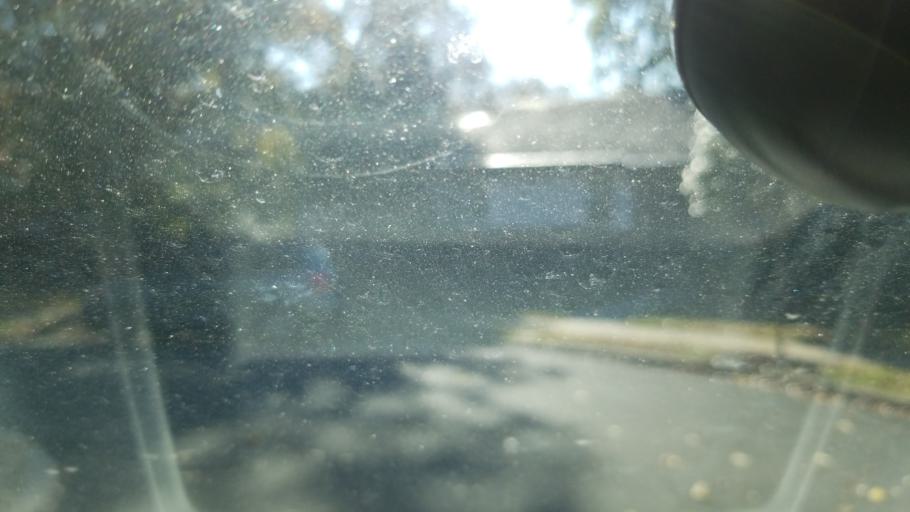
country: US
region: Maryland
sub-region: Montgomery County
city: Chevy Chase
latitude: 38.9486
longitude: -77.0558
